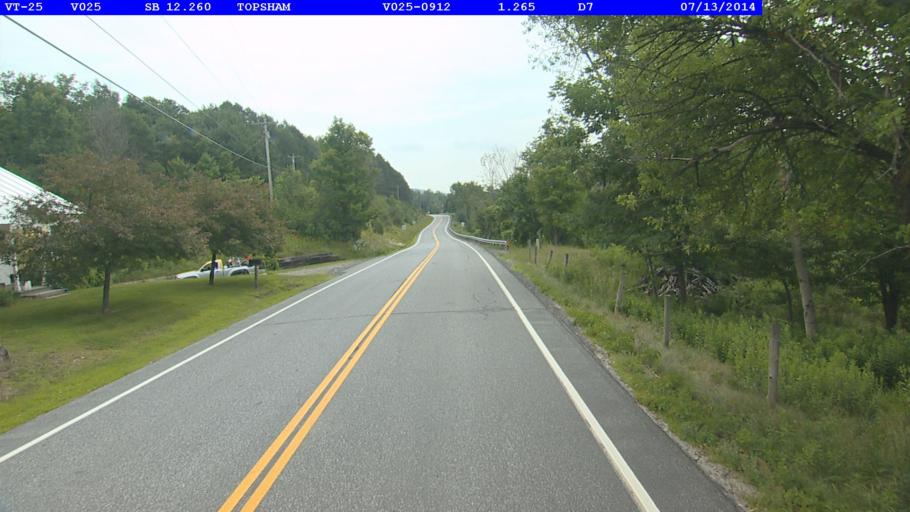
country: US
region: Vermont
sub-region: Orange County
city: Chelsea
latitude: 44.0888
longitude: -72.2809
